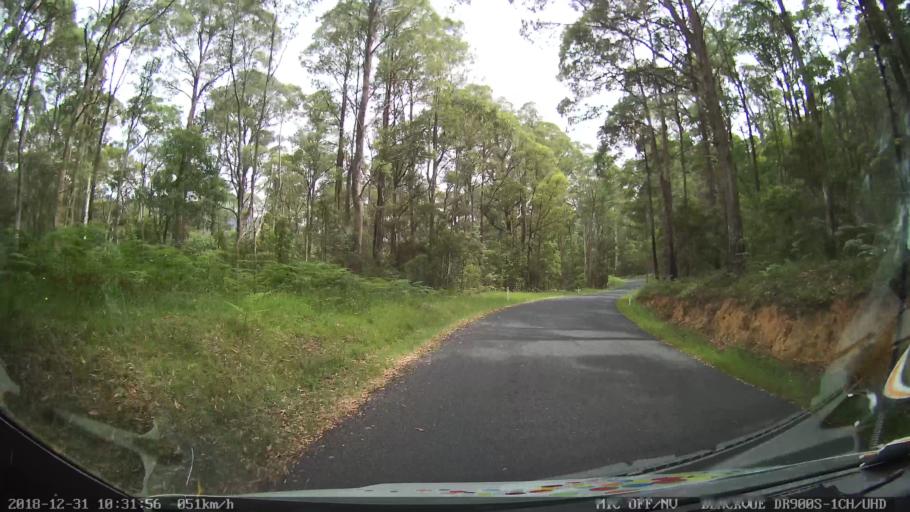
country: AU
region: New South Wales
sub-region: Snowy River
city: Jindabyne
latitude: -36.4544
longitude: 148.1595
